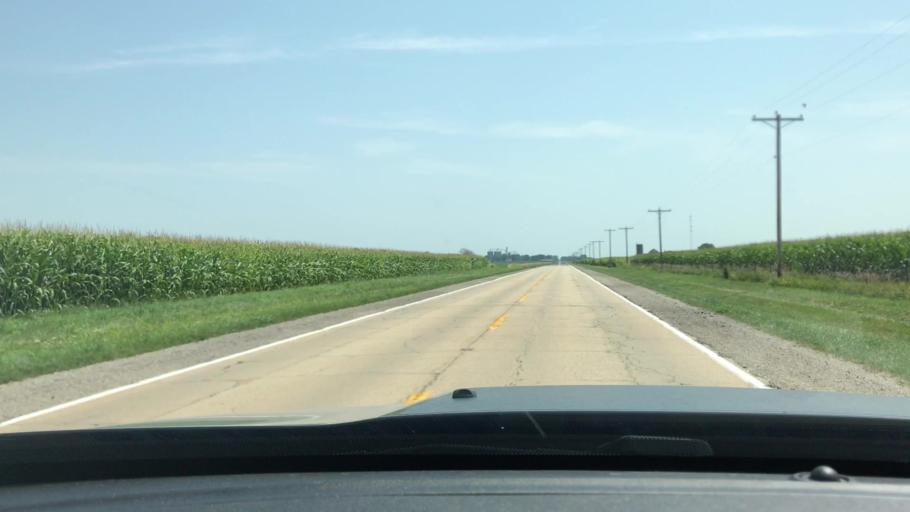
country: US
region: Illinois
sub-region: LaSalle County
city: Sheridan
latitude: 41.4852
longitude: -88.7642
